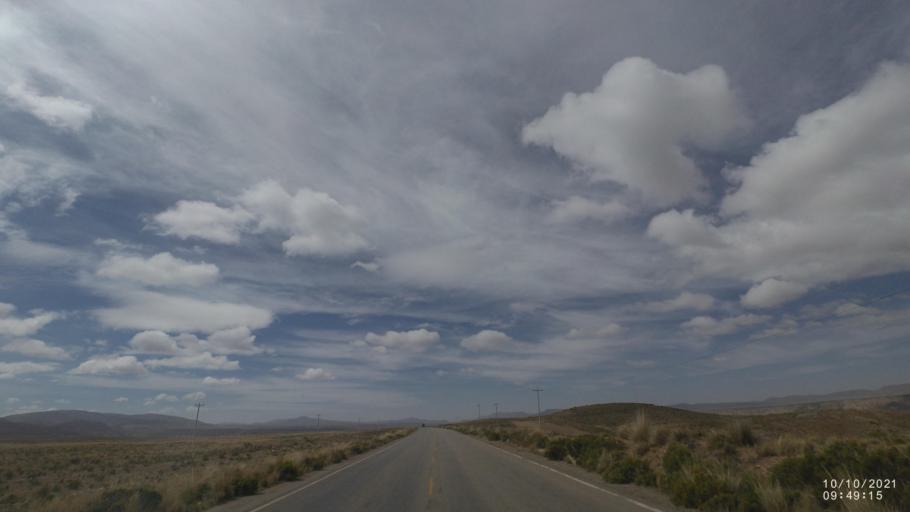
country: BO
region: La Paz
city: Quime
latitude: -17.2234
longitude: -67.3395
